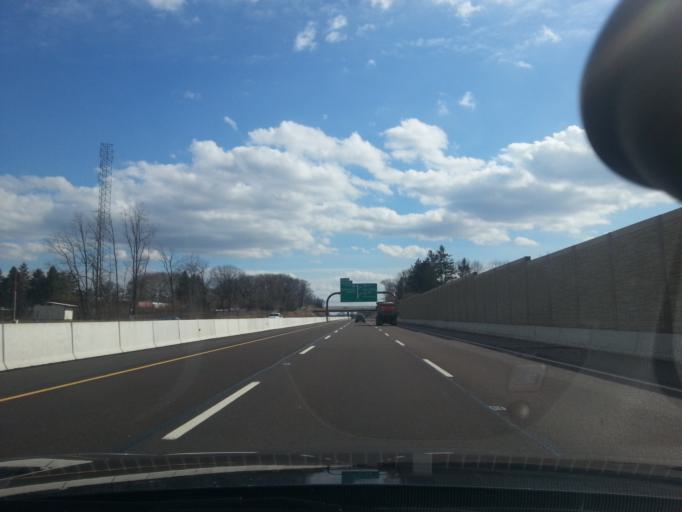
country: US
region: Pennsylvania
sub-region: Montgomery County
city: Blue Bell
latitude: 40.1304
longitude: -75.2857
